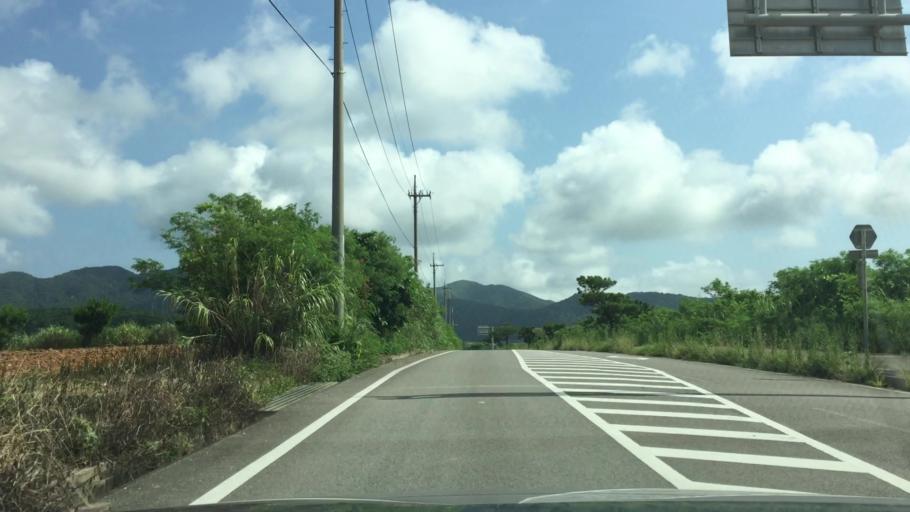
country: JP
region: Okinawa
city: Ishigaki
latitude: 24.4111
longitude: 124.2140
